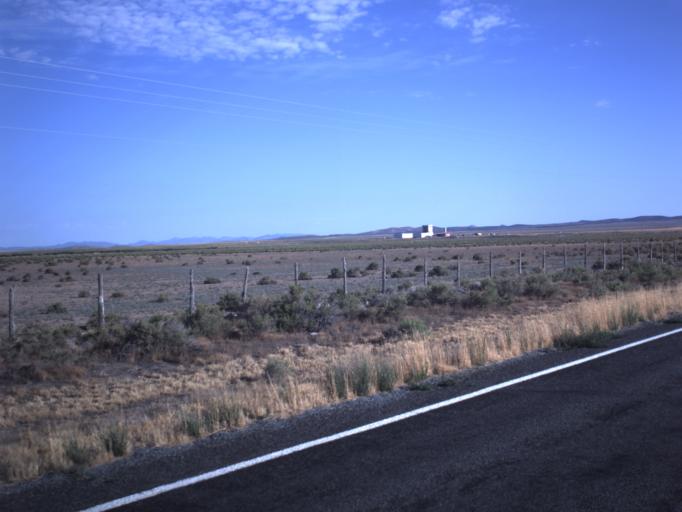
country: US
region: Utah
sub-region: Iron County
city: Enoch
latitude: 37.8623
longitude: -113.0316
